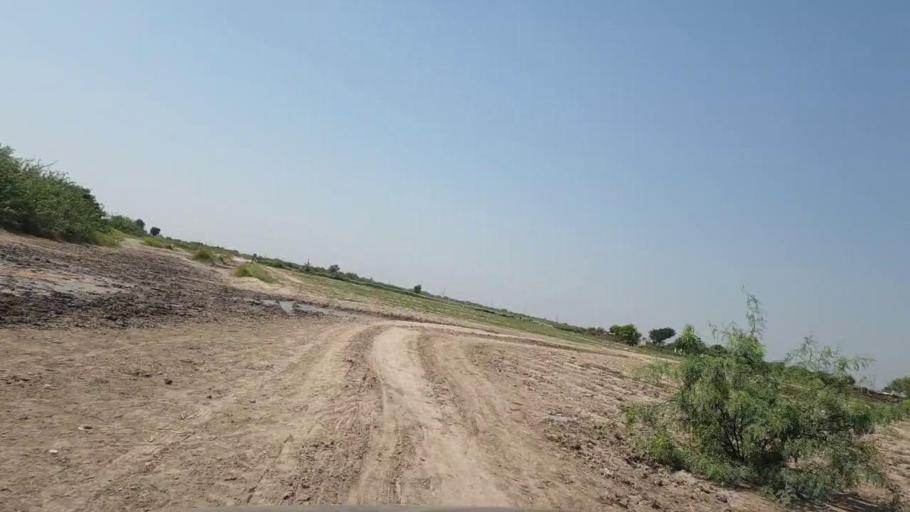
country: PK
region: Sindh
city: Hyderabad
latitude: 25.4679
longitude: 68.4240
